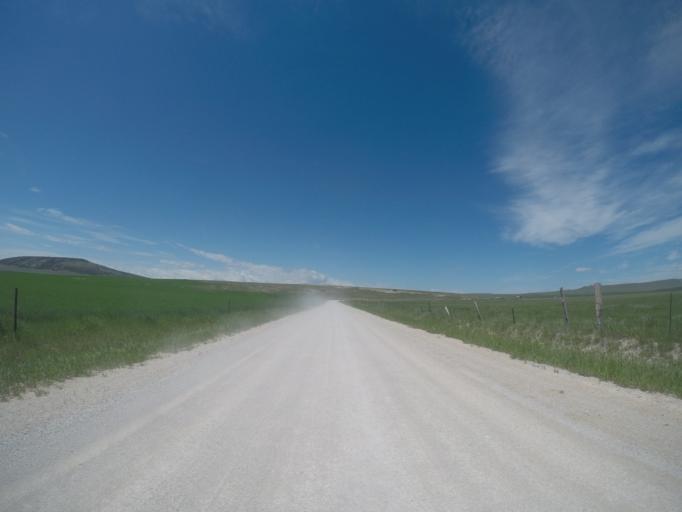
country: US
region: Wyoming
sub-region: Park County
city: Powell
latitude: 45.2050
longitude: -108.7235
